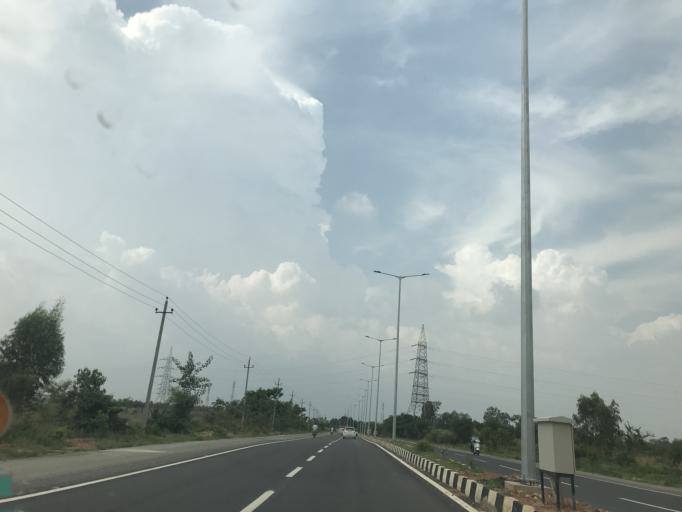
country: IN
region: Karnataka
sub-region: Bangalore Rural
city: Devanhalli
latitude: 13.1644
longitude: 77.6865
